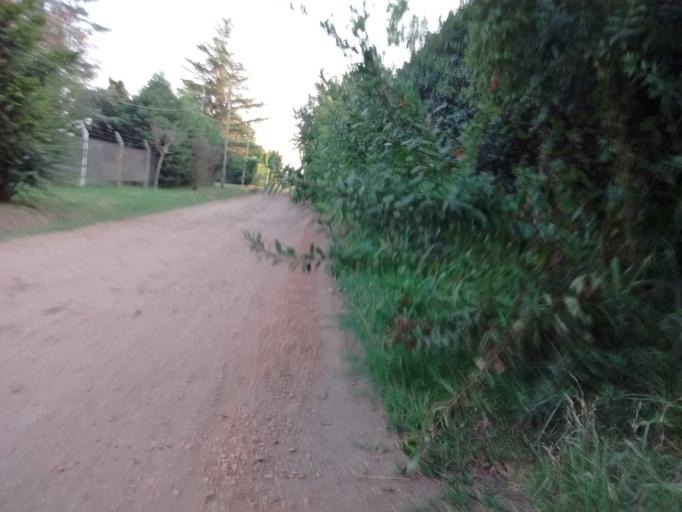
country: AR
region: Santa Fe
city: Funes
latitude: -32.9226
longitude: -60.8346
